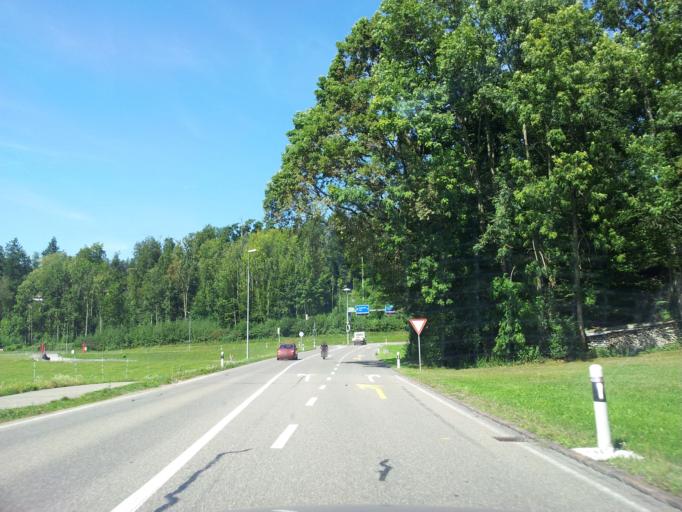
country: CH
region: Saint Gallen
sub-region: Wahlkreis See-Gaster
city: Jona
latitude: 47.2284
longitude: 8.8591
